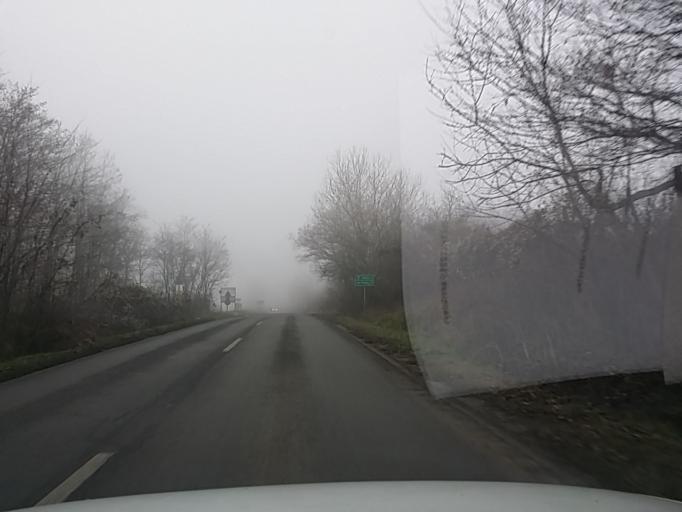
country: HU
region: Pest
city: Telki
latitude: 47.5374
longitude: 18.8455
